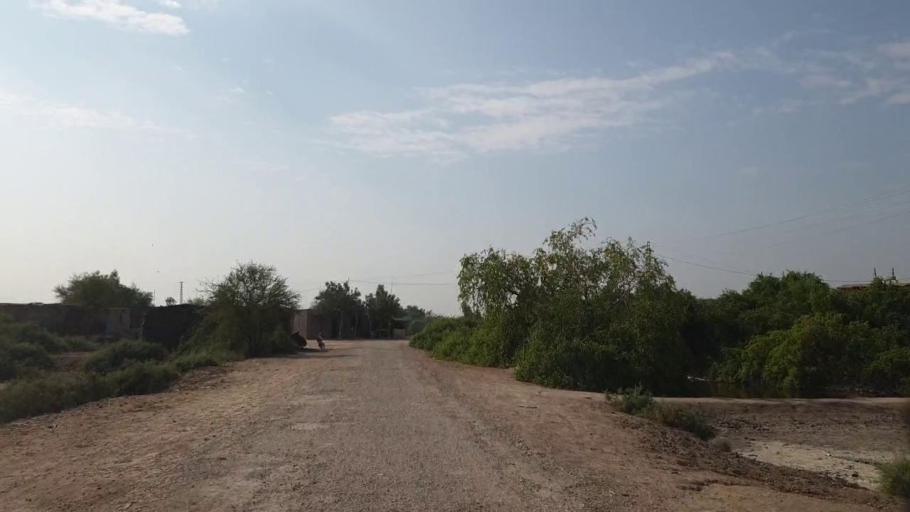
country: PK
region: Sindh
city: Tando Muhammad Khan
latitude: 25.0585
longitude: 68.4132
